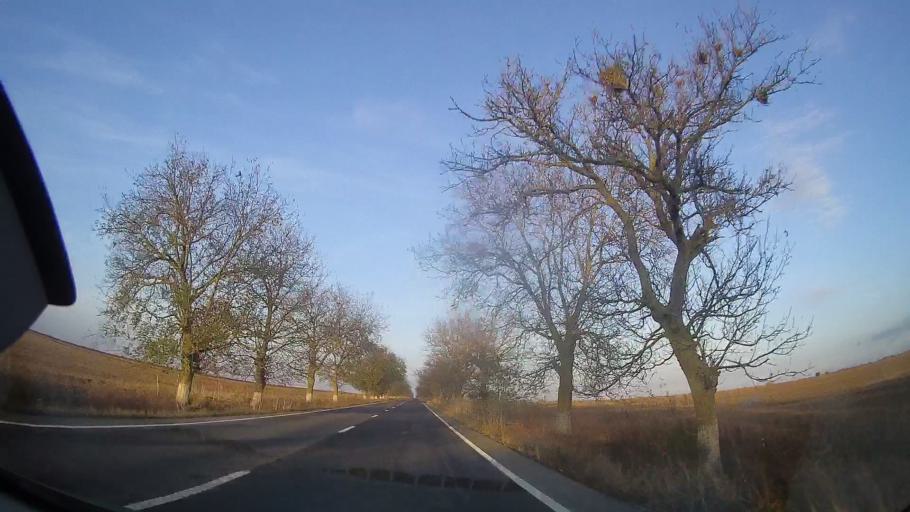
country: RO
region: Constanta
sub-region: Comuna Comana
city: Comana
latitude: 43.9093
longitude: 28.3355
